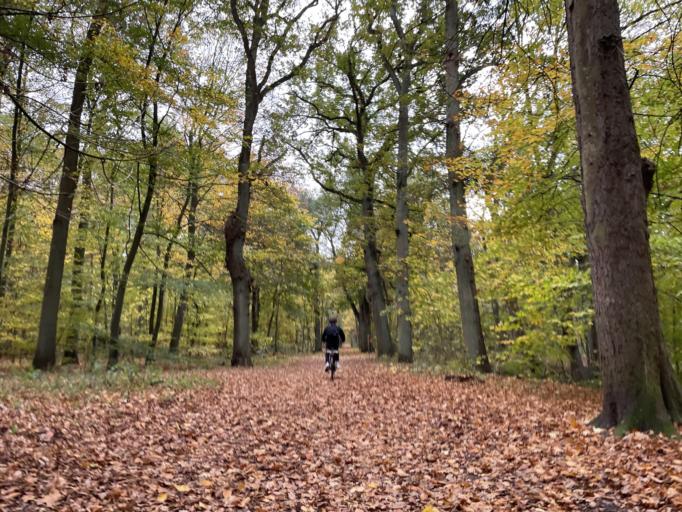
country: DE
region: Lower Saxony
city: Lueneburg
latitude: 53.2223
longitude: 10.3969
